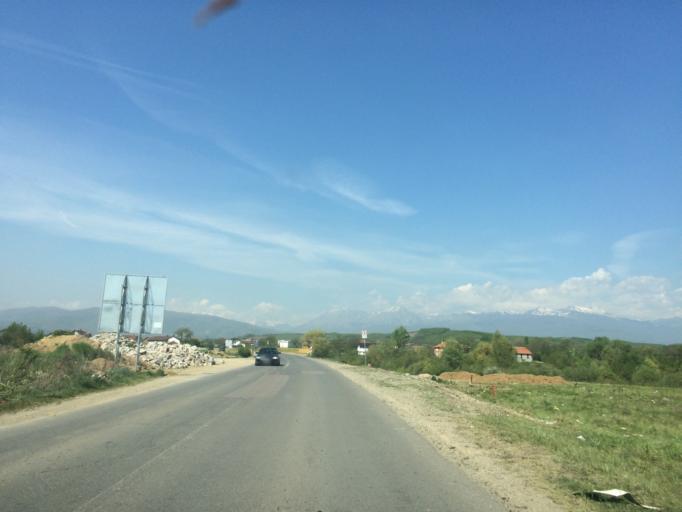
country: XK
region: Gjakova
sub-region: Komuna e Gjakoves
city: Gjakove
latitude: 42.3736
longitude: 20.4079
